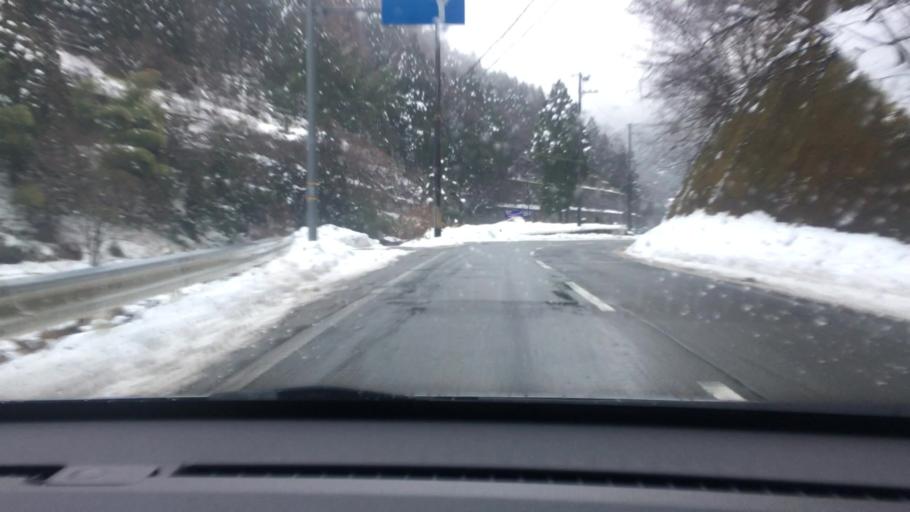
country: JP
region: Hyogo
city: Toyooka
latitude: 35.3670
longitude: 134.5857
